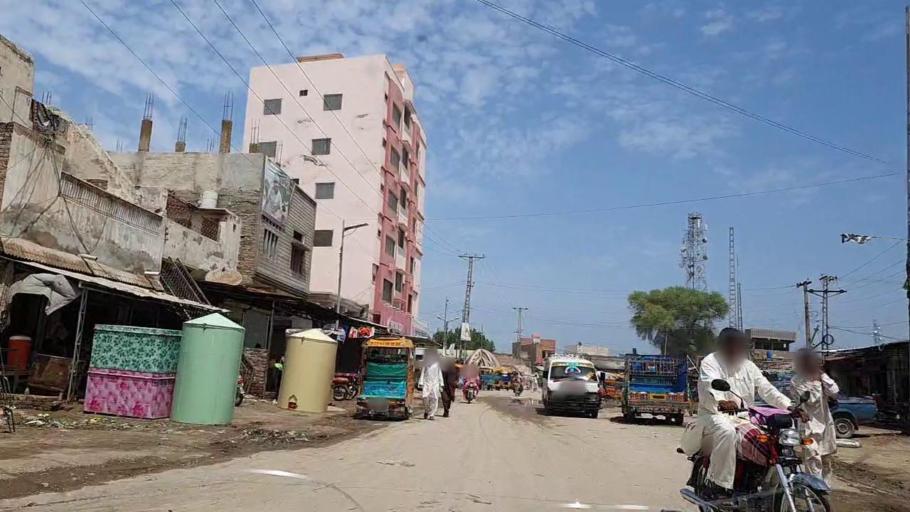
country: PK
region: Sindh
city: Naushahro Firoz
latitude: 26.8423
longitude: 68.1178
